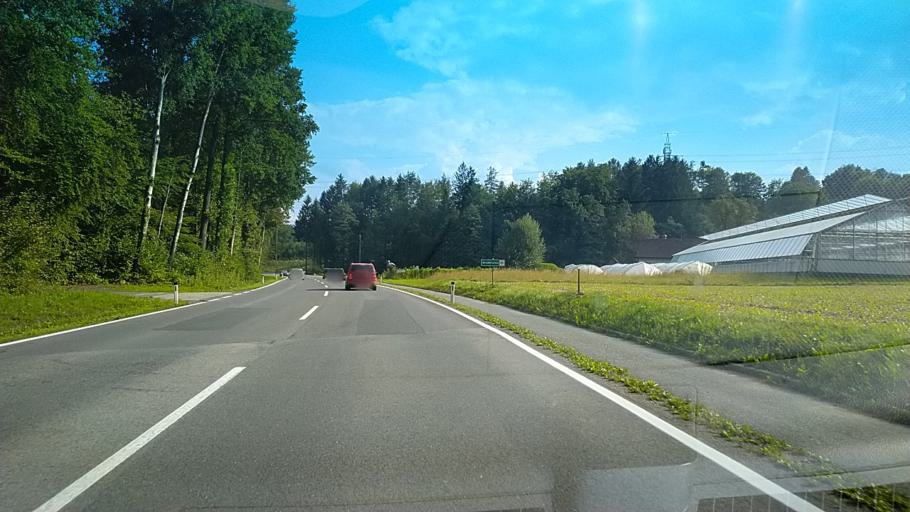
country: AT
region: Styria
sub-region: Politischer Bezirk Deutschlandsberg
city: Hollenegg
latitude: 46.7946
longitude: 15.2204
